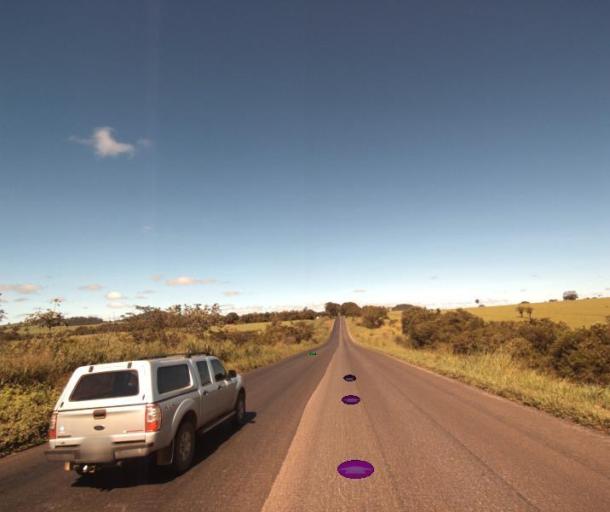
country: BR
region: Goias
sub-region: Itapaci
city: Itapaci
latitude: -15.1272
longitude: -49.5088
